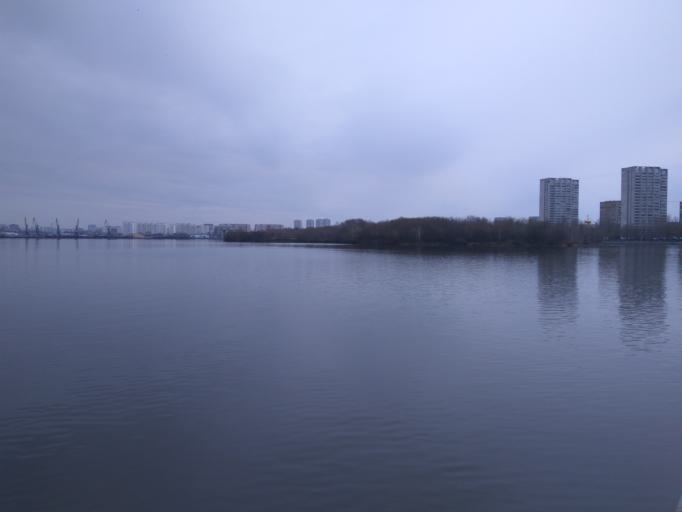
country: RU
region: Moskovskaya
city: Kozhukhovo
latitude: 55.6945
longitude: 37.6858
